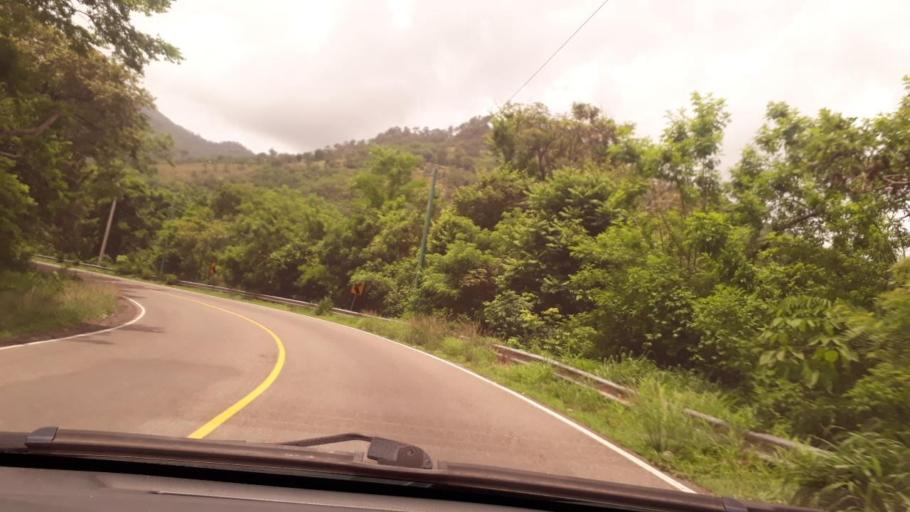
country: GT
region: Chiquimula
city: Quezaltepeque
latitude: 14.6051
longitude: -89.4537
